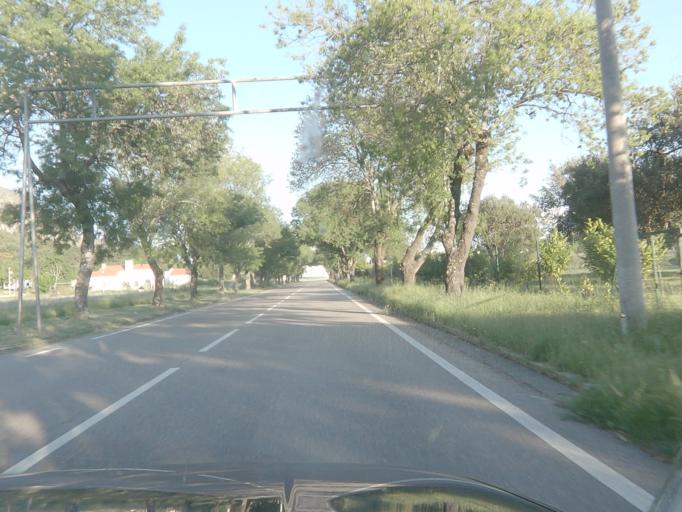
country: PT
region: Portalegre
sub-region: Portalegre
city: Sao Juliao
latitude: 39.3543
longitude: -7.3109
